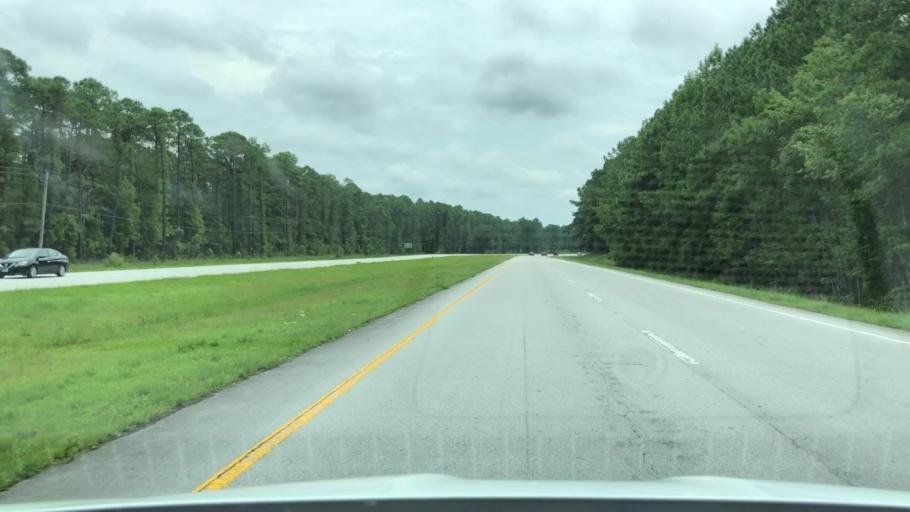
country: US
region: North Carolina
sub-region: Craven County
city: Havelock
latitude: 34.8481
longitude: -76.8859
